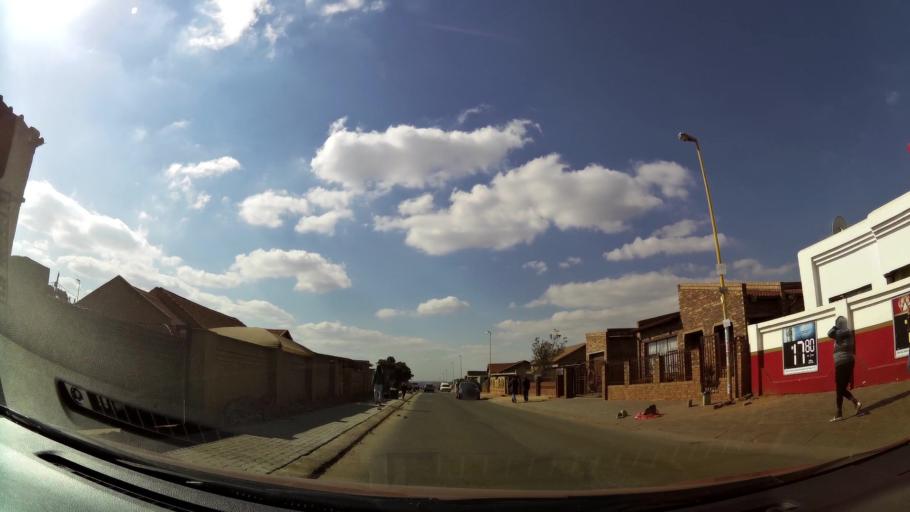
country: ZA
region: Gauteng
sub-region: Ekurhuleni Metropolitan Municipality
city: Tembisa
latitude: -26.0056
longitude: 28.2149
